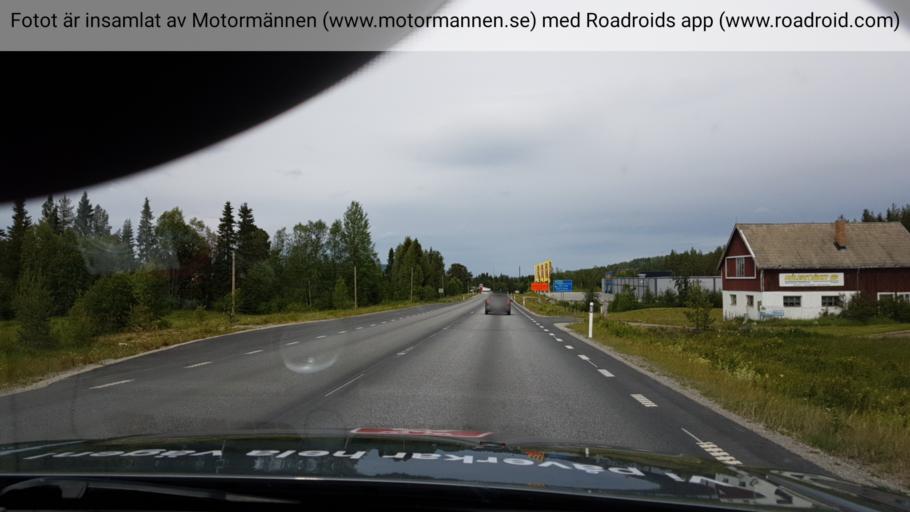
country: SE
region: Jaemtland
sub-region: Bergs Kommun
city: Hoverberg
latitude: 62.7840
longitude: 14.4640
